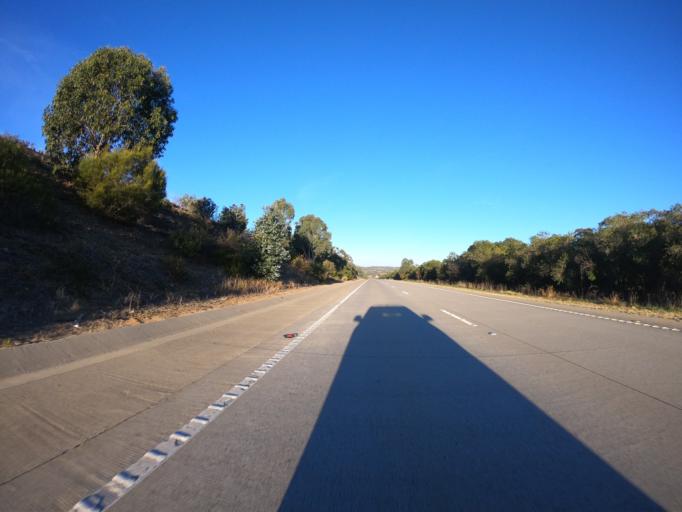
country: AU
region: New South Wales
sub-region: Yass Valley
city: Gundaroo
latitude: -35.1140
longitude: 149.3604
